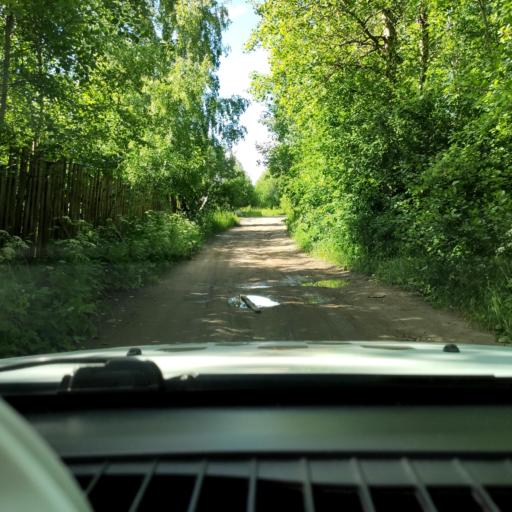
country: RU
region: Perm
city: Overyata
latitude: 58.1044
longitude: 55.8676
